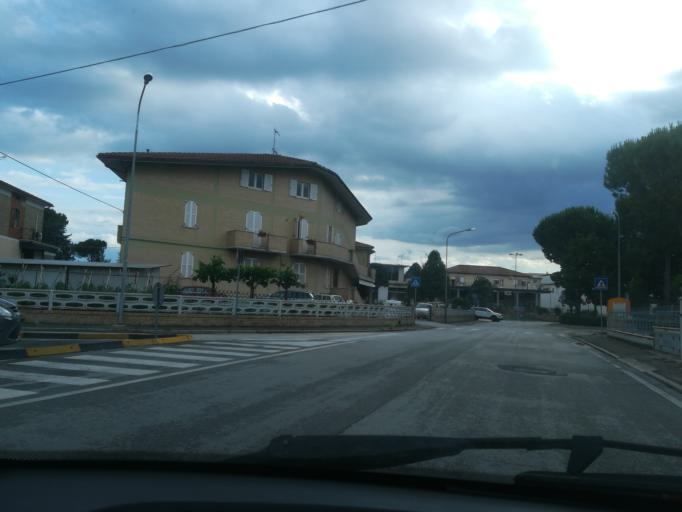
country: IT
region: The Marches
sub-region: Provincia di Macerata
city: Zona Industriale
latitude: 43.2648
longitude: 13.4917
